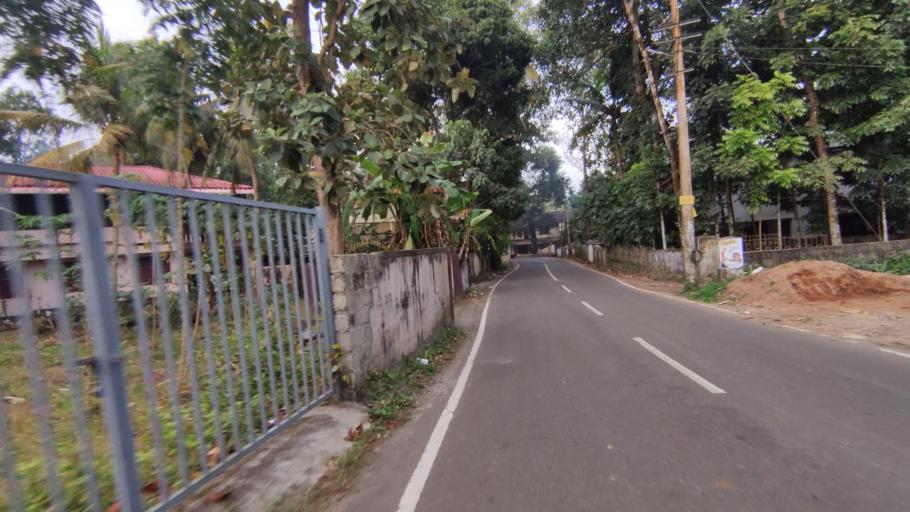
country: IN
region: Kerala
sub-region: Kottayam
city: Kottayam
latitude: 9.6385
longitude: 76.5156
